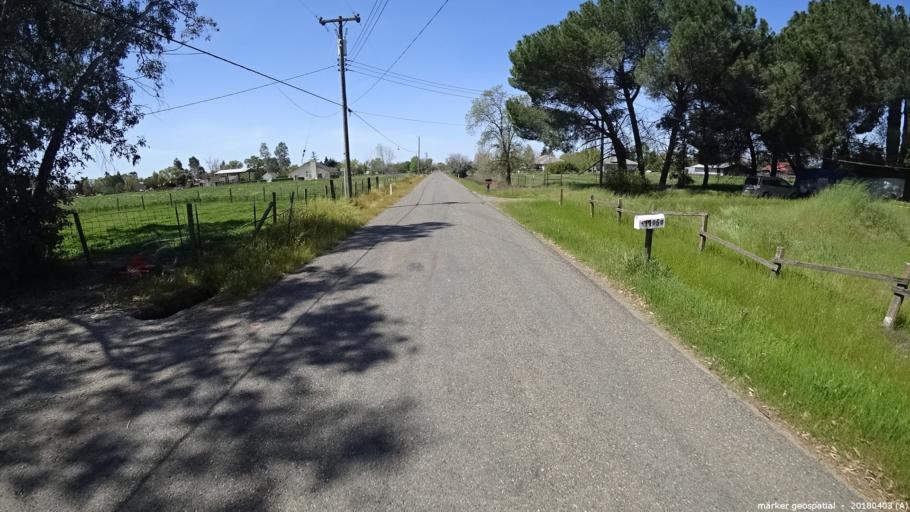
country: US
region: California
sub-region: Sacramento County
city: Wilton
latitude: 38.4021
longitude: -121.2707
